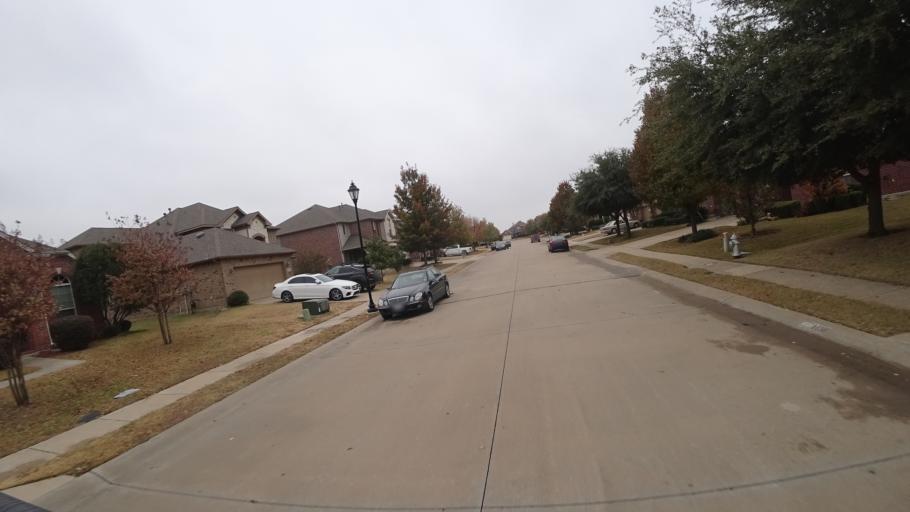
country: US
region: Texas
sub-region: Denton County
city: The Colony
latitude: 33.0692
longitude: -96.9082
